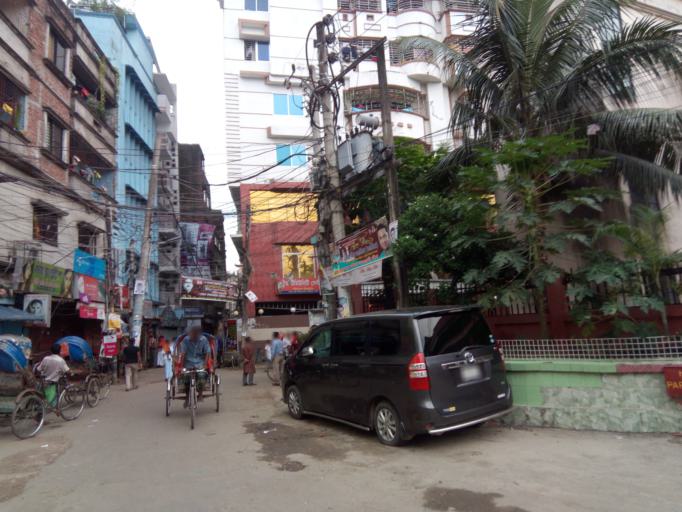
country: BD
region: Dhaka
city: Azimpur
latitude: 23.7218
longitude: 90.3905
